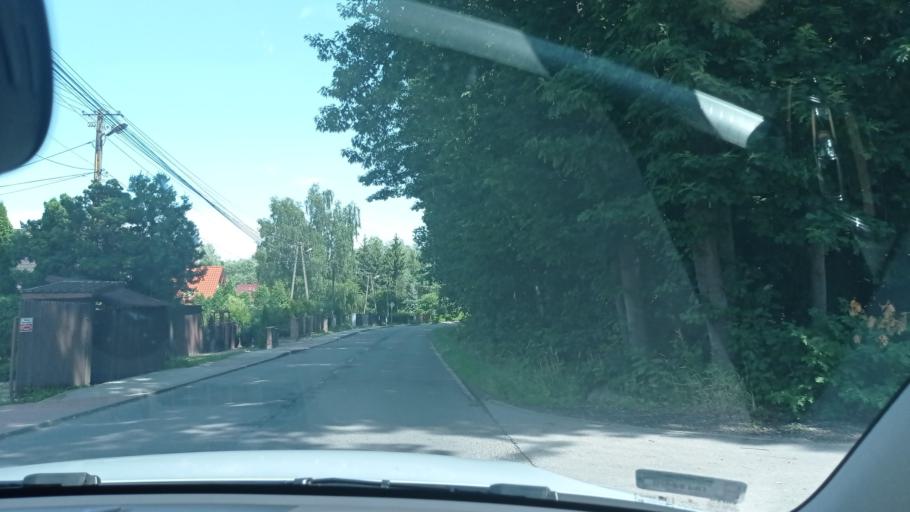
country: PL
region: Lesser Poland Voivodeship
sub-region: Powiat wielicki
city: Wegrzce Wielkie
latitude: 50.0148
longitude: 20.1243
